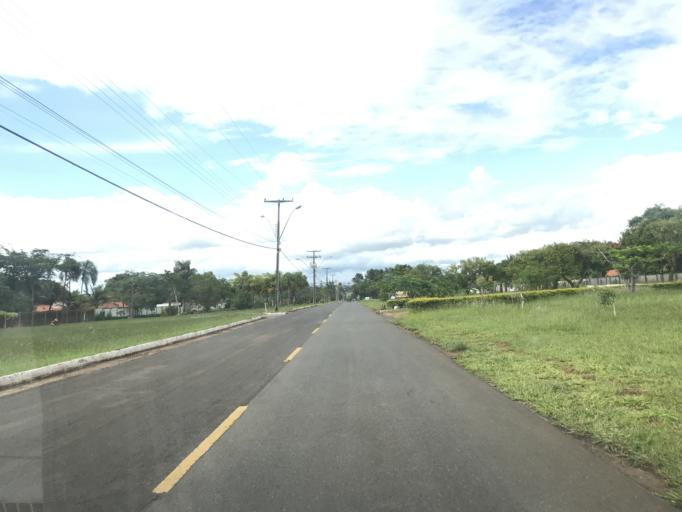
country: BR
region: Federal District
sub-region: Brasilia
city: Brasilia
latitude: -15.8988
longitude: -47.9201
